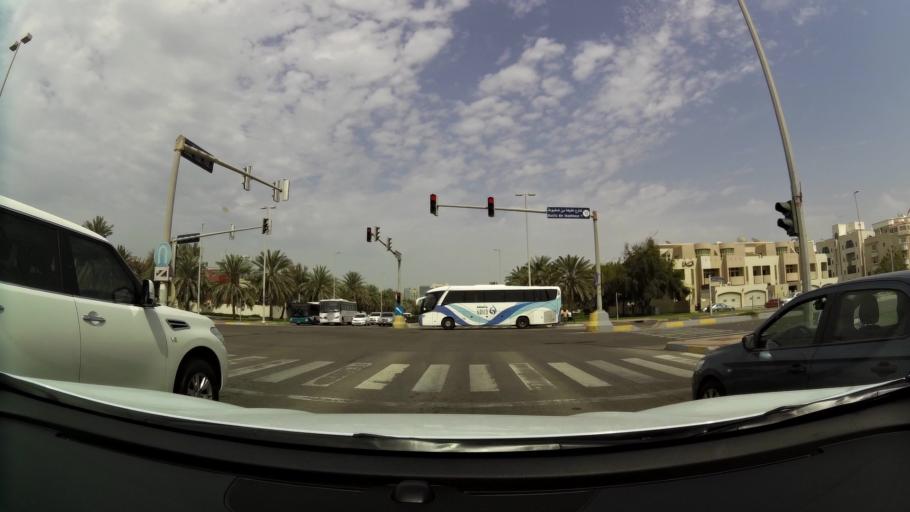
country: AE
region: Abu Dhabi
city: Abu Dhabi
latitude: 24.4590
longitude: 54.3582
